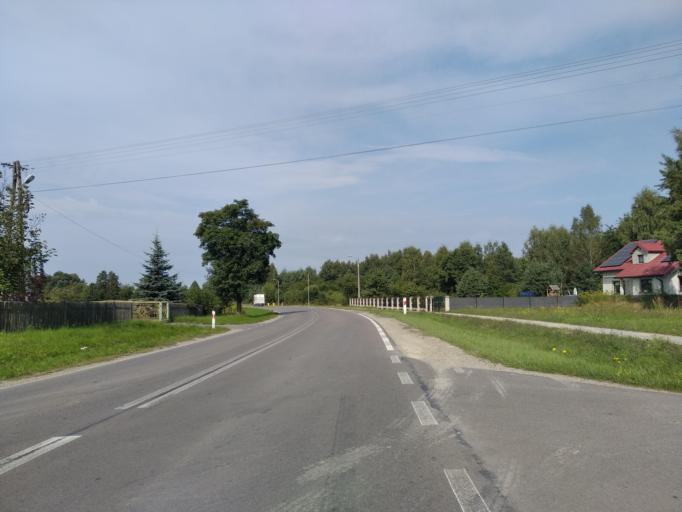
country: PL
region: Subcarpathian Voivodeship
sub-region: Powiat mielecki
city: Przeclaw
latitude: 50.1609
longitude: 21.5315
